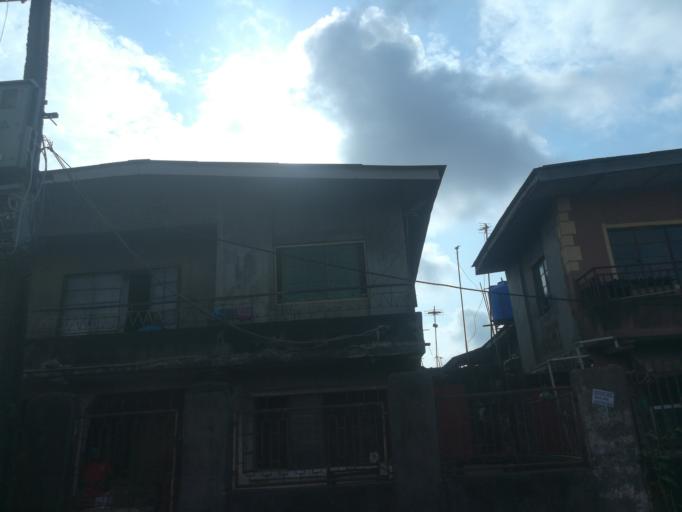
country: NG
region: Lagos
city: Agege
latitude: 6.6162
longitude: 3.3141
